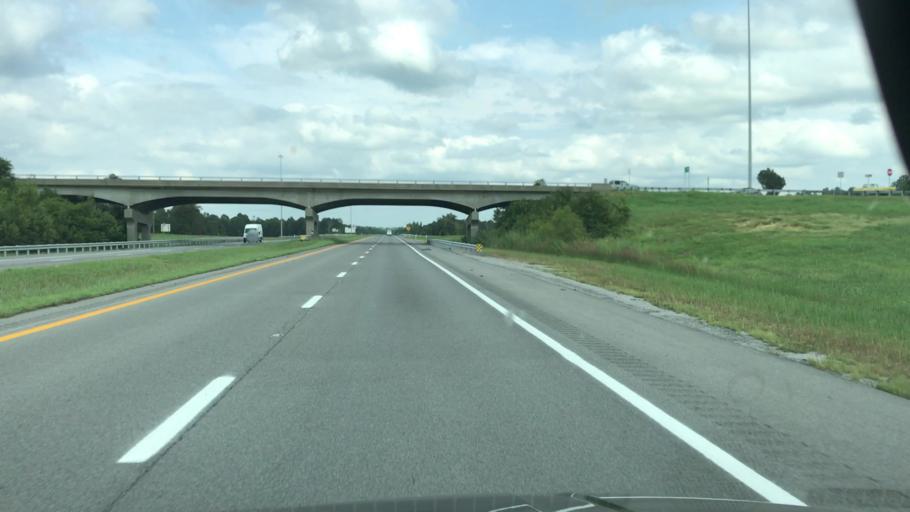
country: US
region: Kentucky
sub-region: Hopkins County
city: Dawson Springs
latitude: 37.1979
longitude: -87.6903
